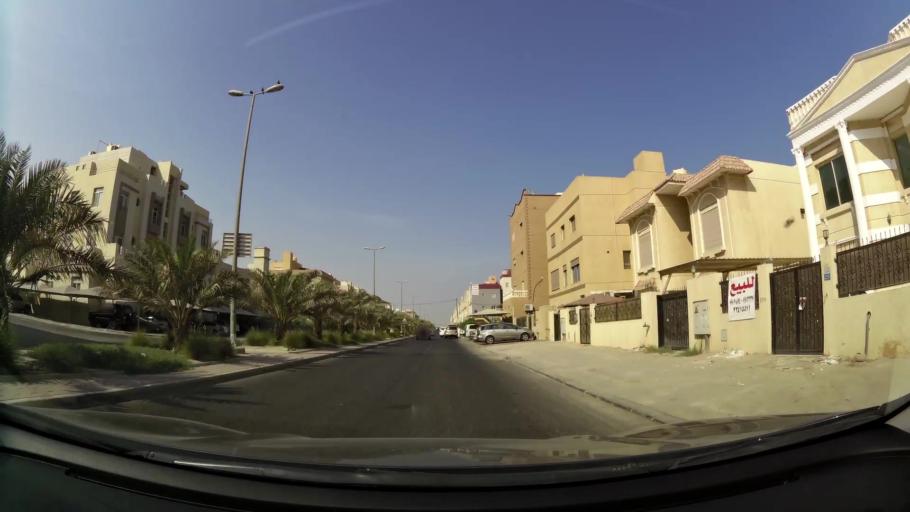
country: KW
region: Al Ahmadi
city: Al Manqaf
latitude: 29.1124
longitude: 48.1230
